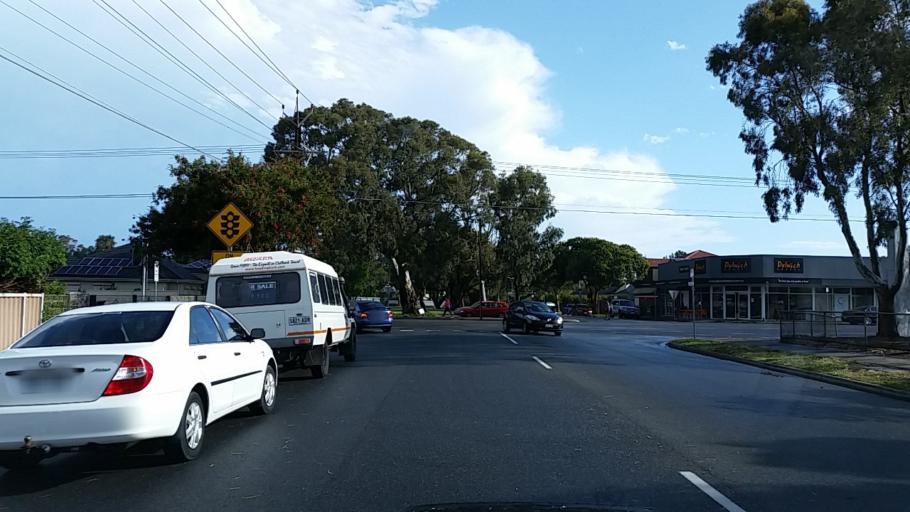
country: AU
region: South Australia
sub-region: Charles Sturt
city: Henley Beach
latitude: -34.9249
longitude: 138.5014
